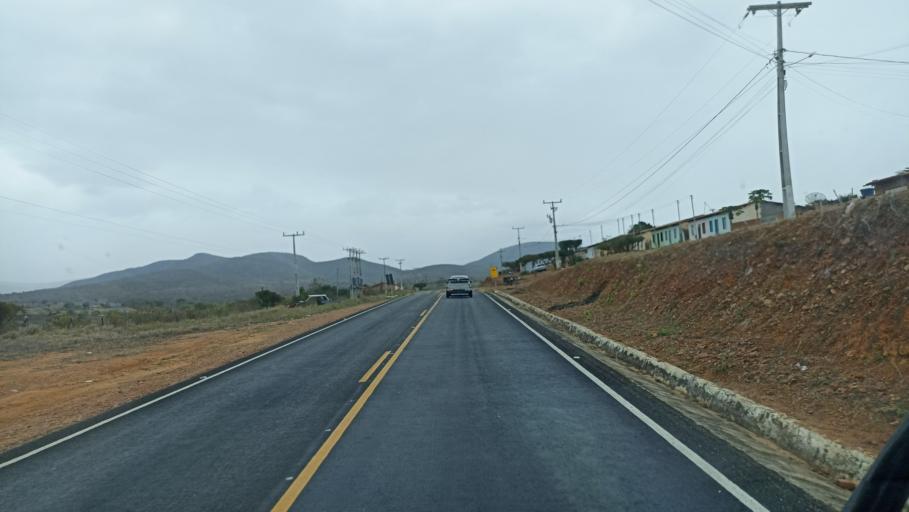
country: BR
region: Bahia
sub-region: Maracas
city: Maracas
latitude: -13.0482
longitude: -40.7432
